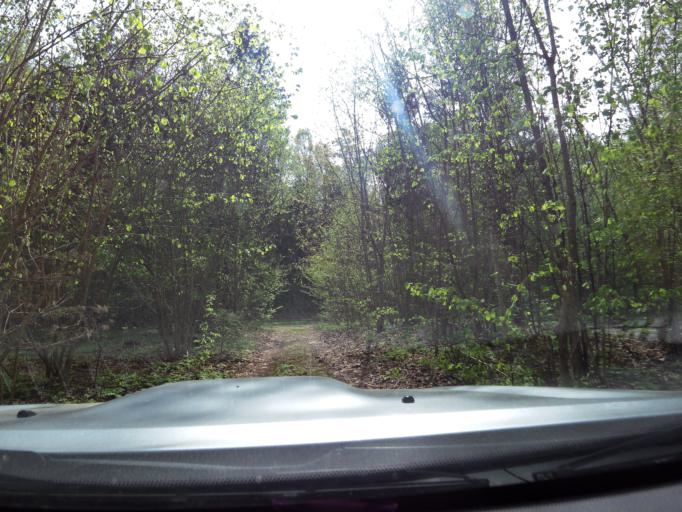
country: LT
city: Salcininkai
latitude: 54.4242
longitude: 25.3063
